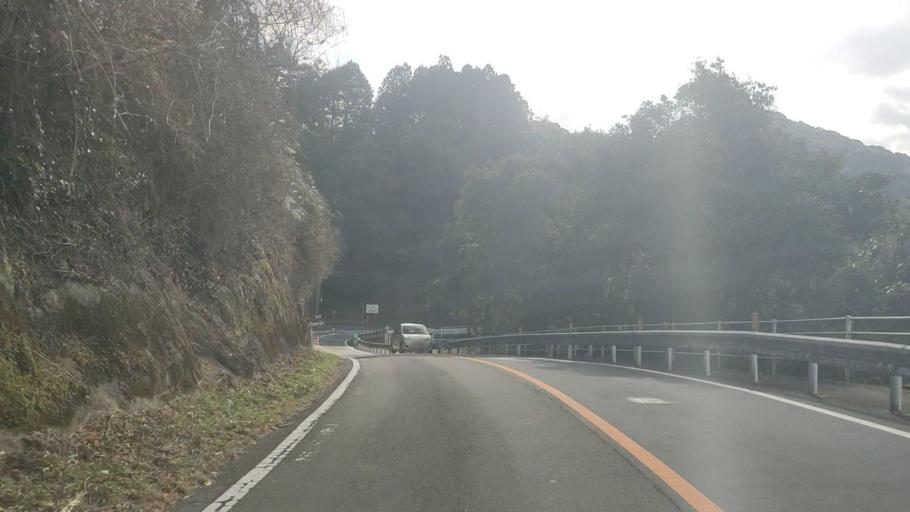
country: JP
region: Kumamoto
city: Hitoyoshi
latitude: 32.2894
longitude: 130.8457
